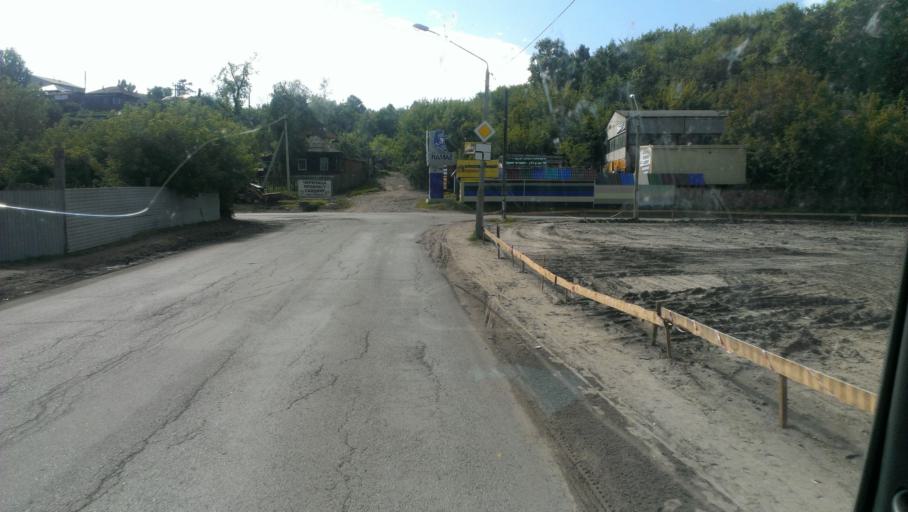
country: RU
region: Altai Krai
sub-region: Gorod Barnaulskiy
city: Barnaul
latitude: 53.3196
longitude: 83.7703
